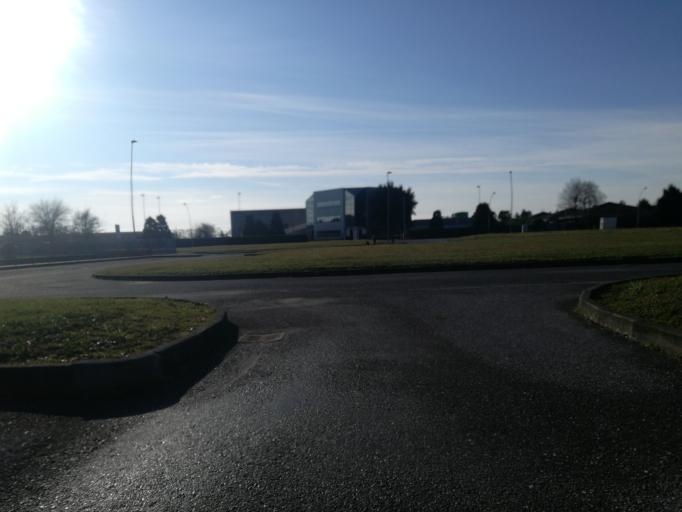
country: IT
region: Lombardy
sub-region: Provincia di Monza e Brianza
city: Sulbiate
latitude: 45.6463
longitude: 9.4311
